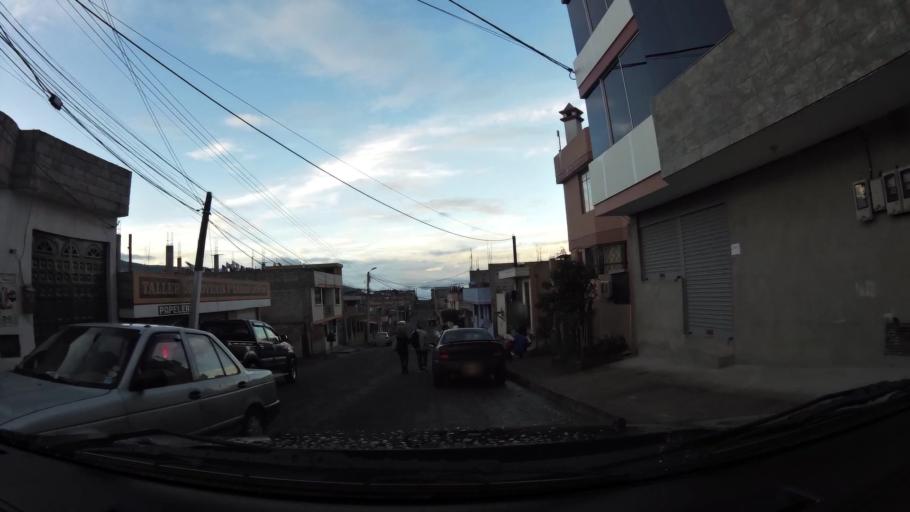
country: EC
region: Pichincha
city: Quito
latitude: -0.0978
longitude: -78.5186
